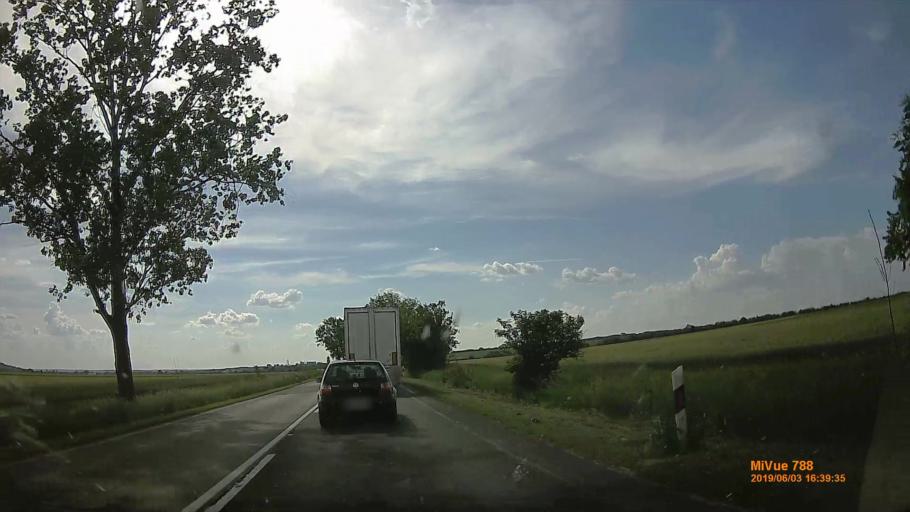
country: HU
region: Fejer
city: Cece
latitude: 46.7649
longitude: 18.5920
